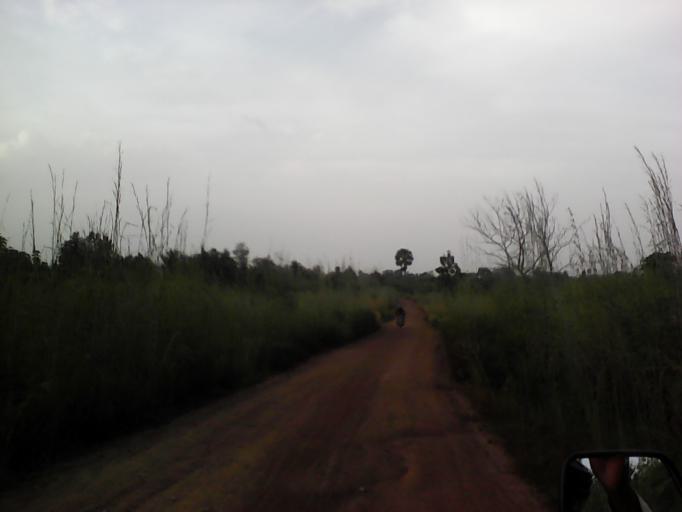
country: TG
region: Centrale
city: Sotouboua
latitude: 8.2260
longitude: 0.9771
